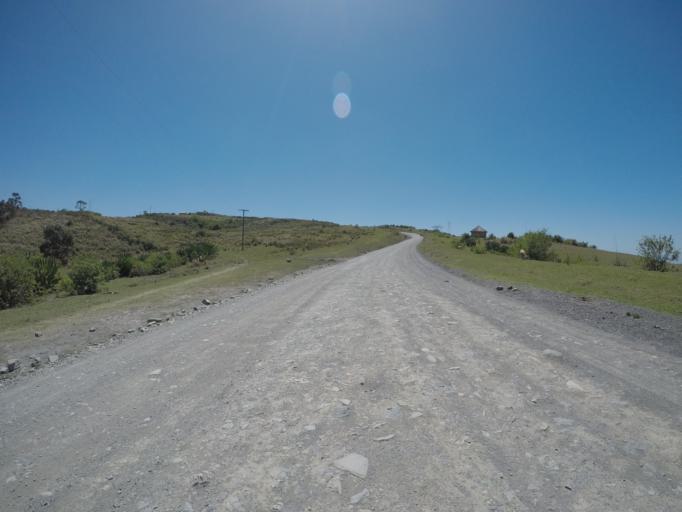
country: ZA
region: Eastern Cape
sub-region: OR Tambo District Municipality
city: Libode
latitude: -31.9786
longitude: 29.0350
